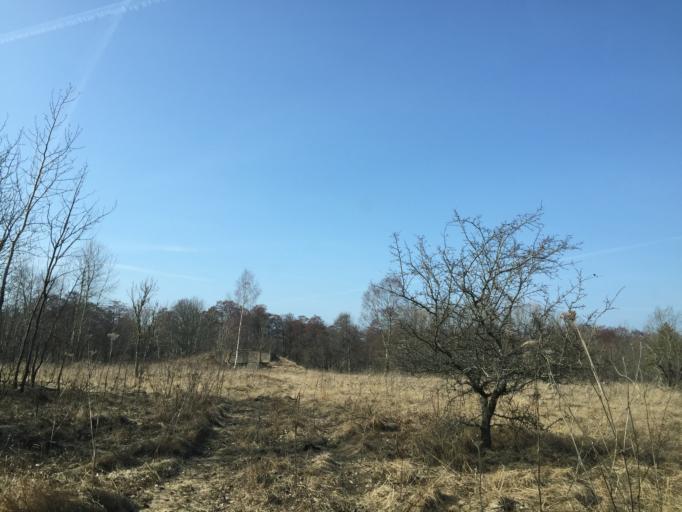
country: LV
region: Dundaga
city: Dundaga
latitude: 57.9241
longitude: 22.0608
